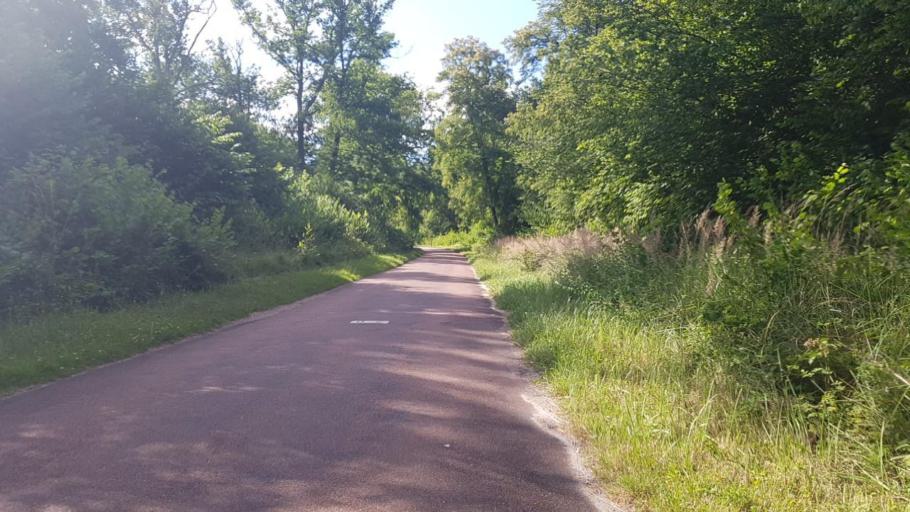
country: FR
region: Picardie
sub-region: Departement de l'Oise
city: Chamant
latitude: 49.1791
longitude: 2.6201
